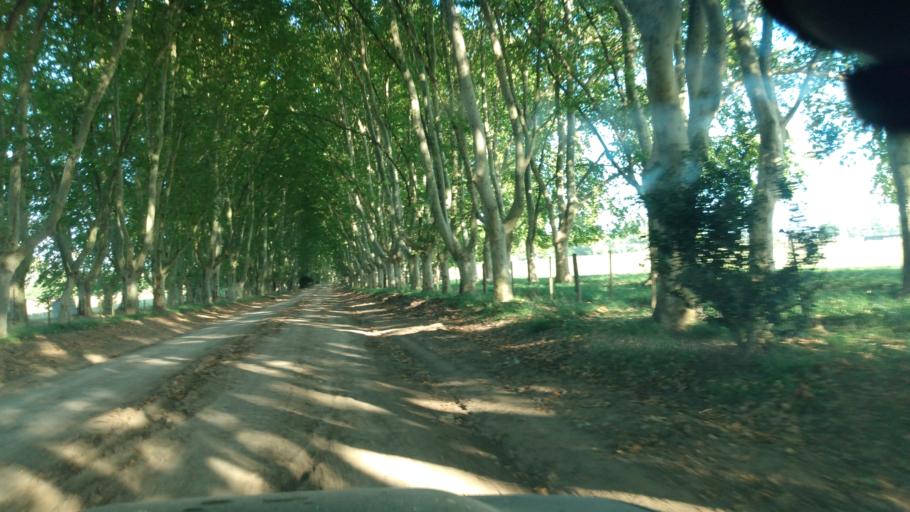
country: AR
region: Buenos Aires
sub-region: Partido de Lujan
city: Lujan
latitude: -34.5816
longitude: -59.0817
